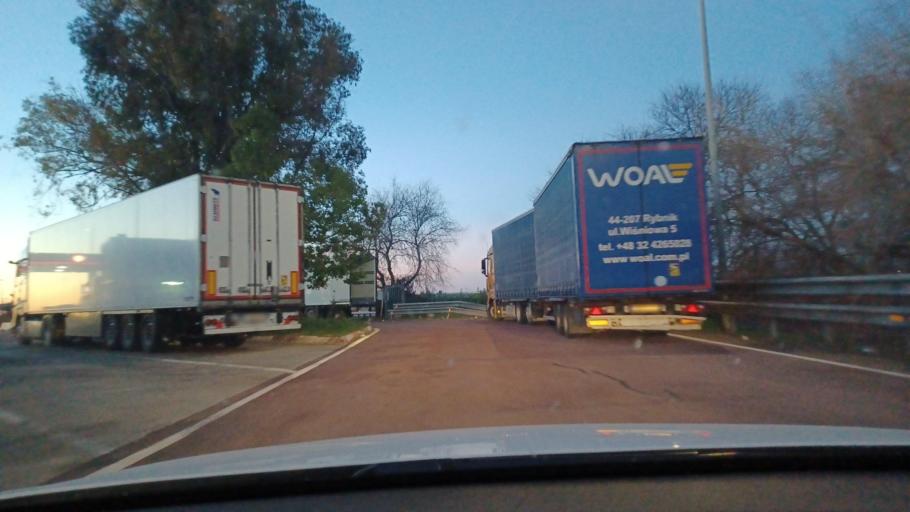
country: ES
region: Valencia
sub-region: Provincia de Castello
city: Alquerias del Nino Perdido
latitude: 39.8643
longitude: -0.1244
